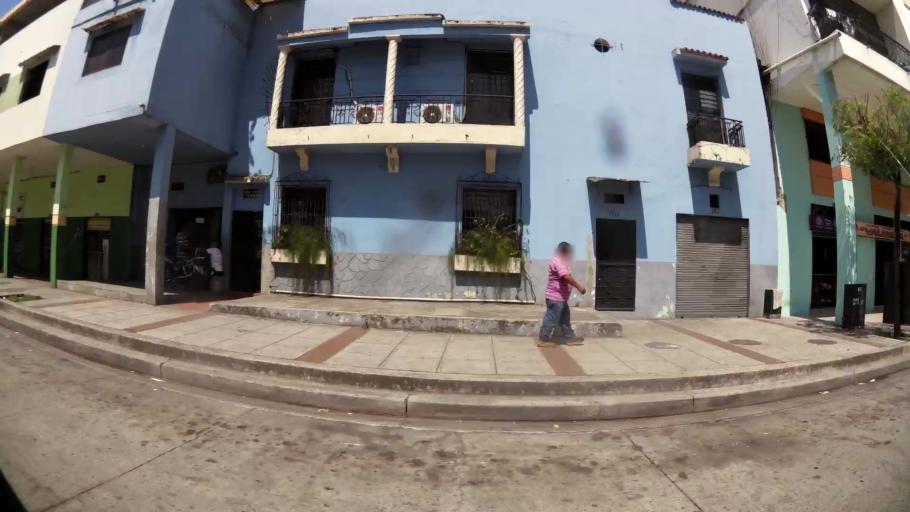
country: EC
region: Guayas
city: Guayaquil
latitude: -2.1949
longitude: -79.8957
